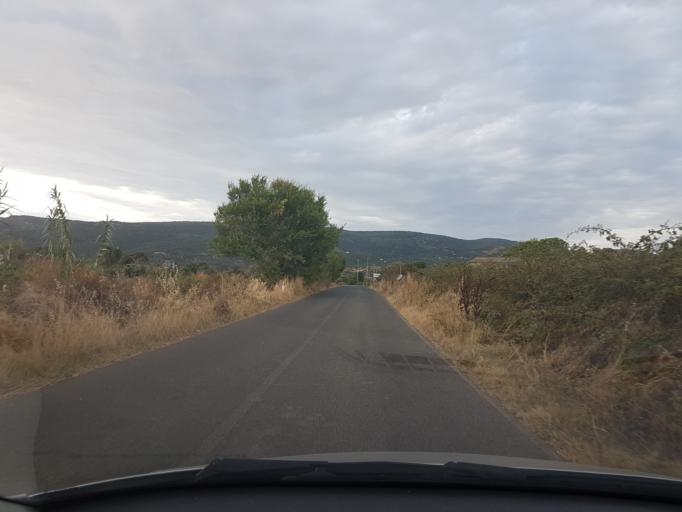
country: IT
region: Sardinia
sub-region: Provincia di Oristano
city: Seneghe
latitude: 40.0779
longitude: 8.6070
